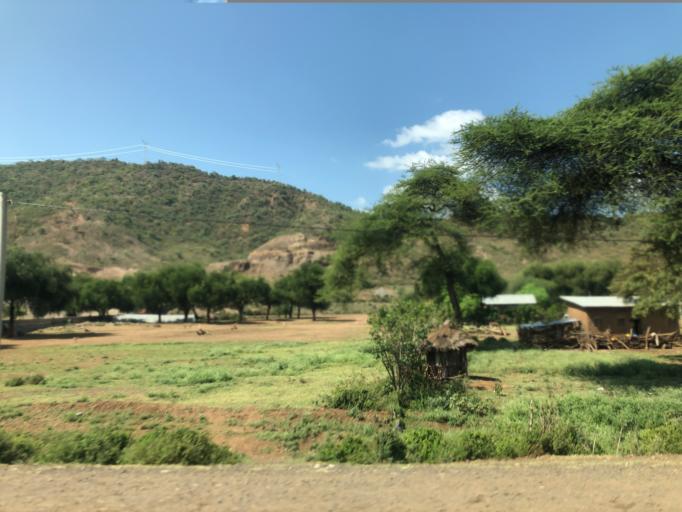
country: ET
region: Southern Nations, Nationalities, and People's Region
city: Gidole
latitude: 5.8191
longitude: 37.4562
